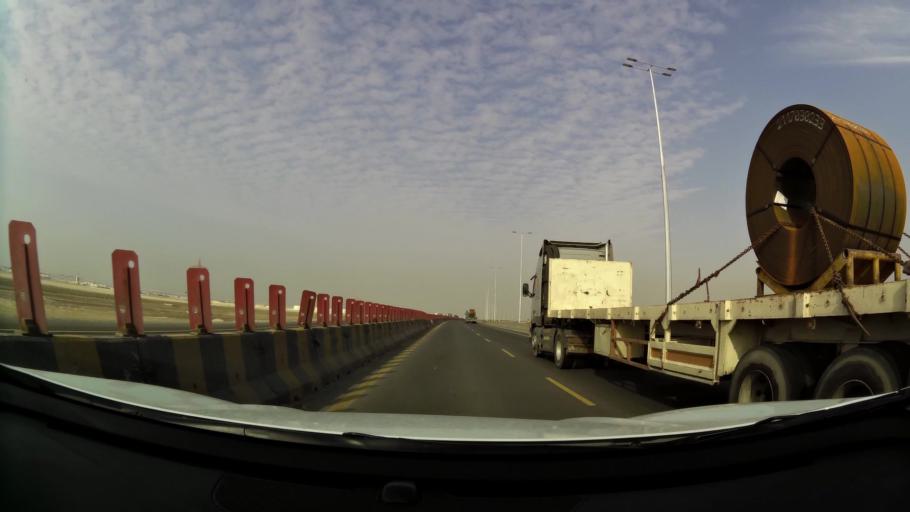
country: AE
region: Abu Dhabi
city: Abu Dhabi
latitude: 24.2643
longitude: 54.4922
